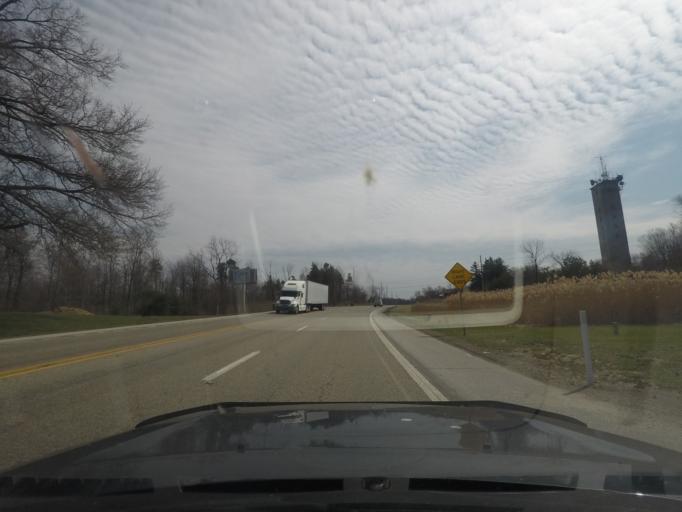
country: US
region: Indiana
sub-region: LaPorte County
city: LaPorte
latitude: 41.6583
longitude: -86.7664
